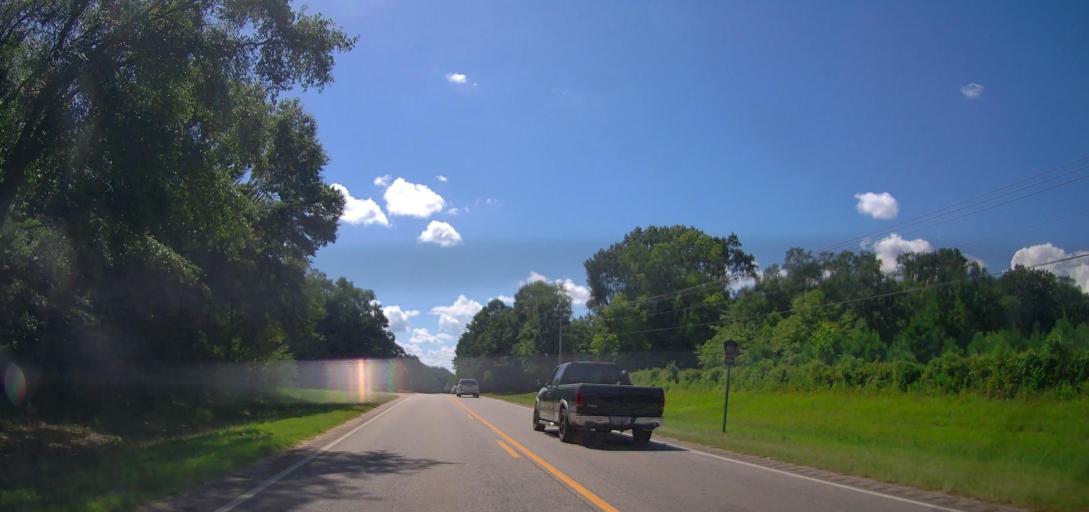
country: US
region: Alabama
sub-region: Elmore County
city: Tallassee
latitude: 32.3785
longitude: -85.8618
